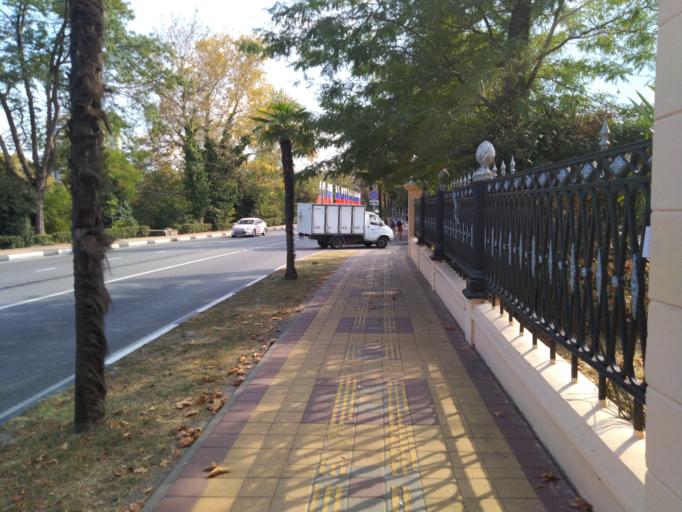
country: RU
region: Krasnodarskiy
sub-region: Sochi City
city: Sochi
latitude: 43.5909
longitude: 39.7171
